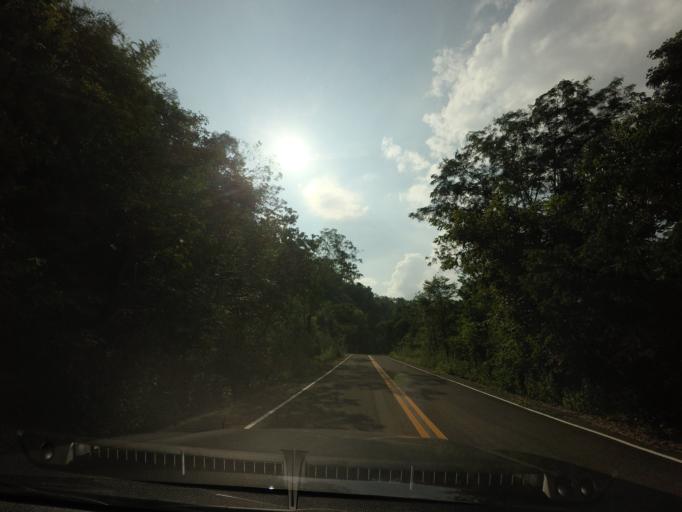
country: TH
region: Nan
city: Na Noi
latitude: 18.2759
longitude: 100.9616
